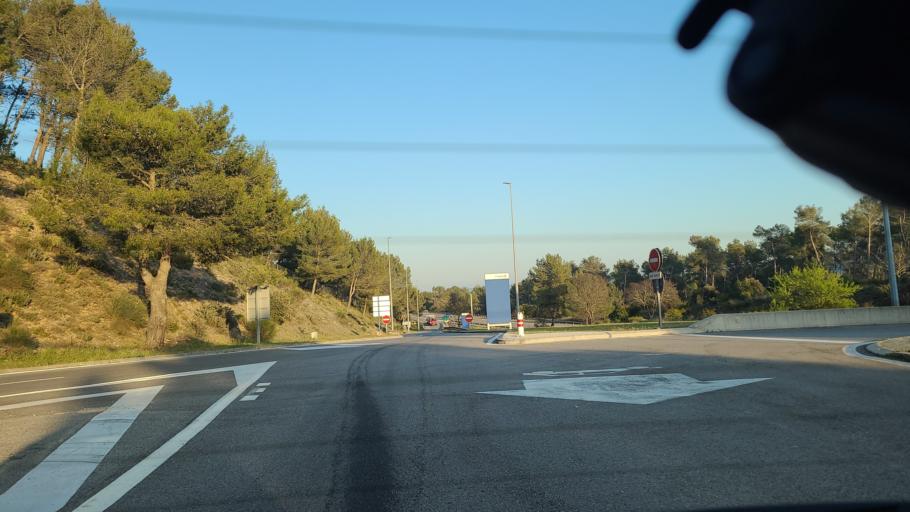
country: FR
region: Provence-Alpes-Cote d'Azur
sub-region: Departement du Var
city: La Celle
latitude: 43.4235
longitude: 5.9937
